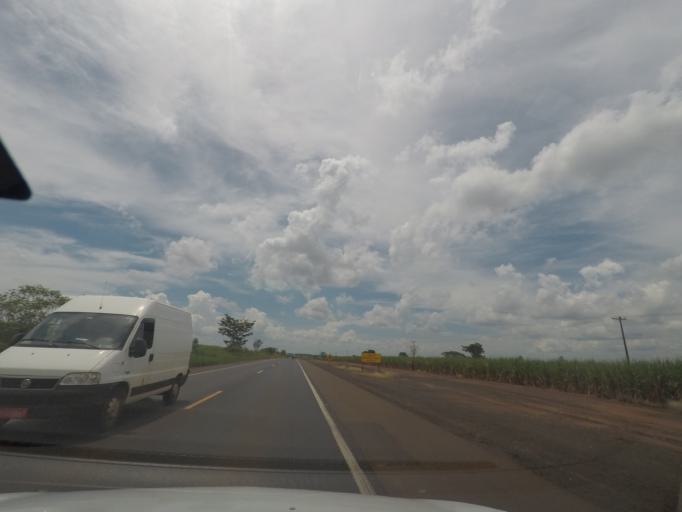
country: BR
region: Sao Paulo
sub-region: Barretos
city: Barretos
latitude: -20.3888
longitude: -48.6402
